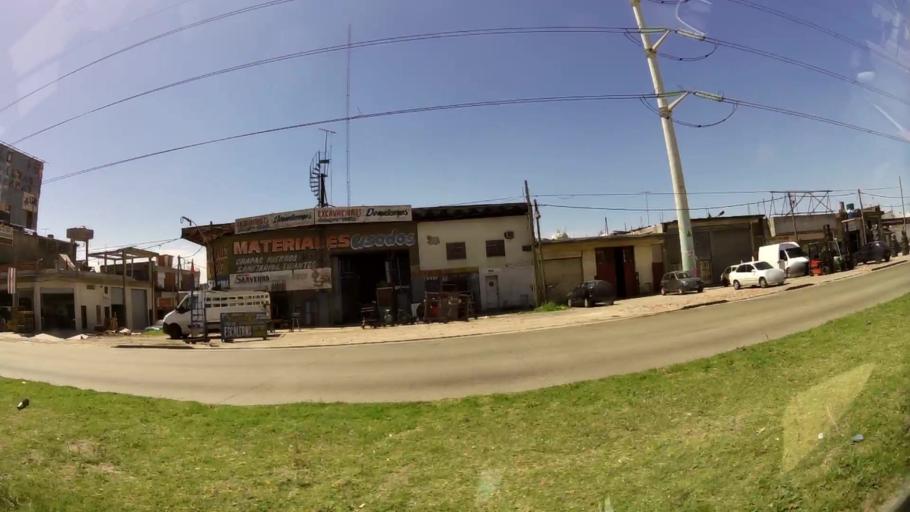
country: AR
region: Buenos Aires
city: Caseros
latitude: -34.5627
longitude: -58.5809
